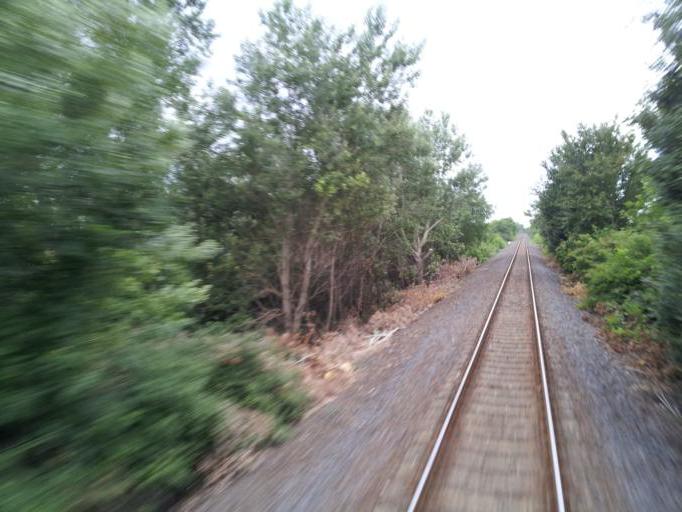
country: HU
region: Fejer
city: Polgardi
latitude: 47.0787
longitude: 18.3413
